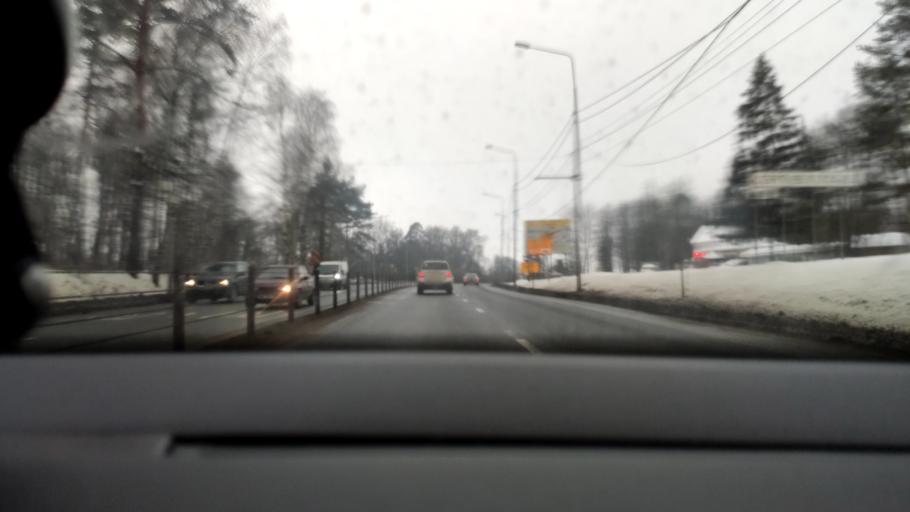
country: RU
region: Moskovskaya
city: Sergiyev Posad
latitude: 56.2675
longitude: 38.1225
